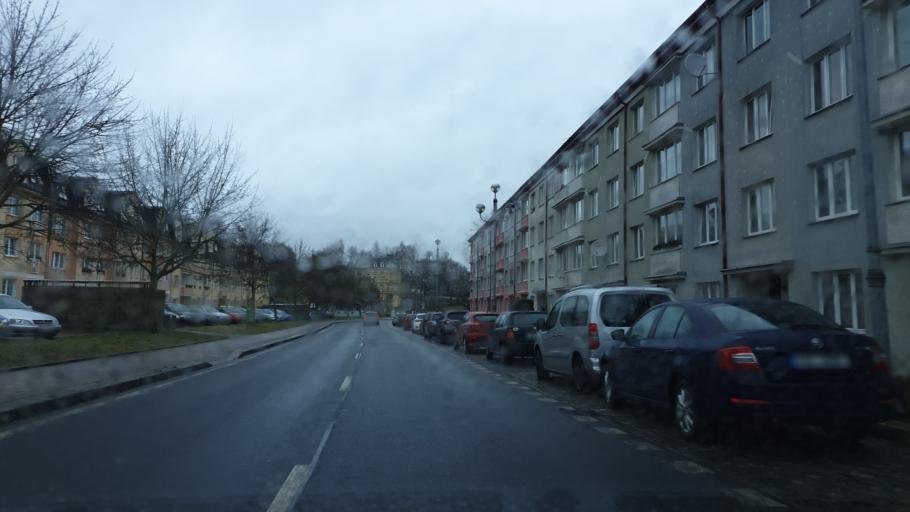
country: CZ
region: Karlovarsky
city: As
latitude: 50.2233
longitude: 12.1868
